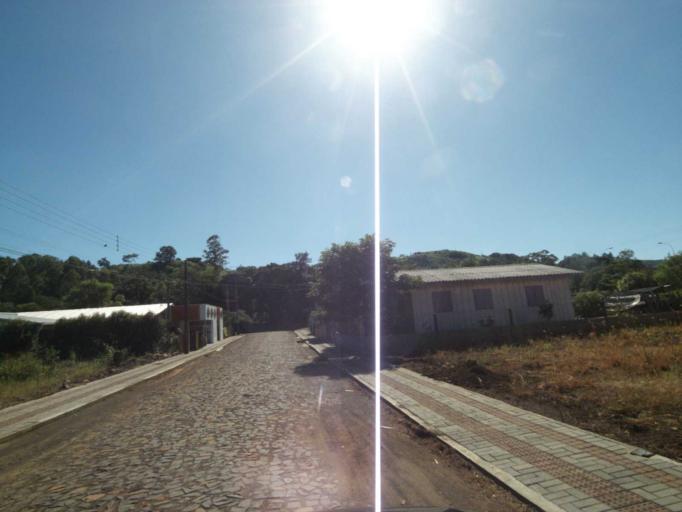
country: BR
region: Parana
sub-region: Francisco Beltrao
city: Francisco Beltrao
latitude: -26.1430
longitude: -53.3093
